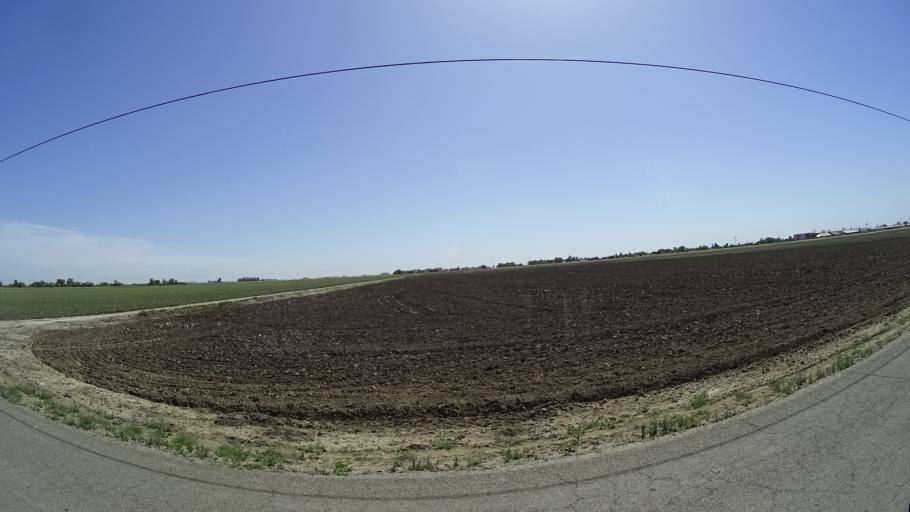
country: US
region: California
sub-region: Kings County
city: Stratford
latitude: 36.2003
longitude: -119.8340
